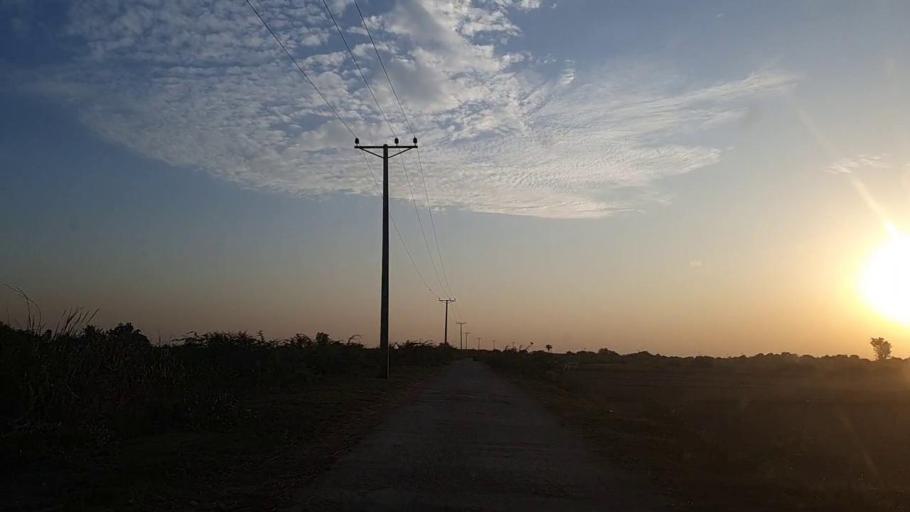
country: PK
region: Sindh
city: Thatta
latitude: 24.7959
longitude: 67.9410
